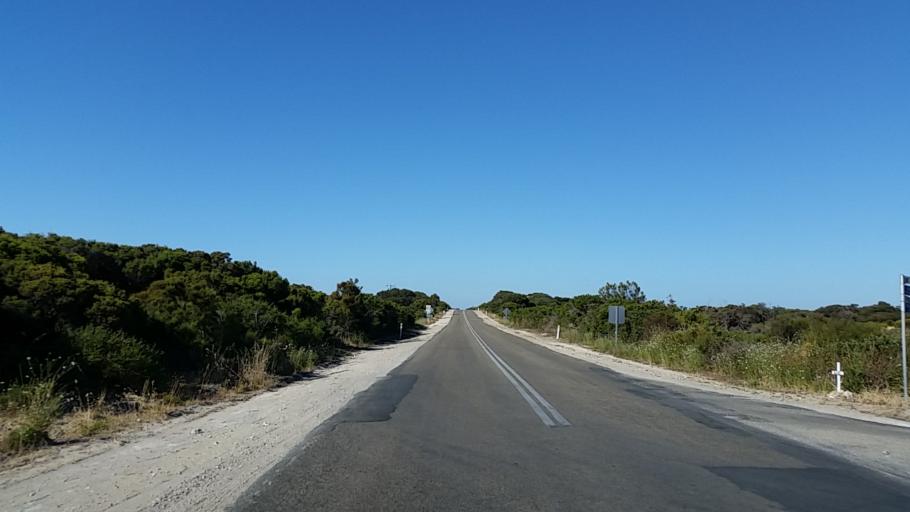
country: AU
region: South Australia
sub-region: Yorke Peninsula
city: Honiton
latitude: -35.2439
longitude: 136.9741
